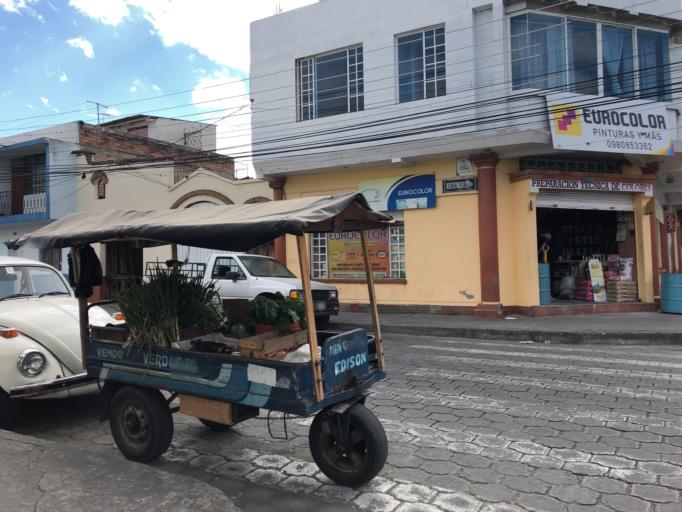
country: EC
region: Imbabura
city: Ibarra
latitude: 0.3499
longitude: -78.1241
